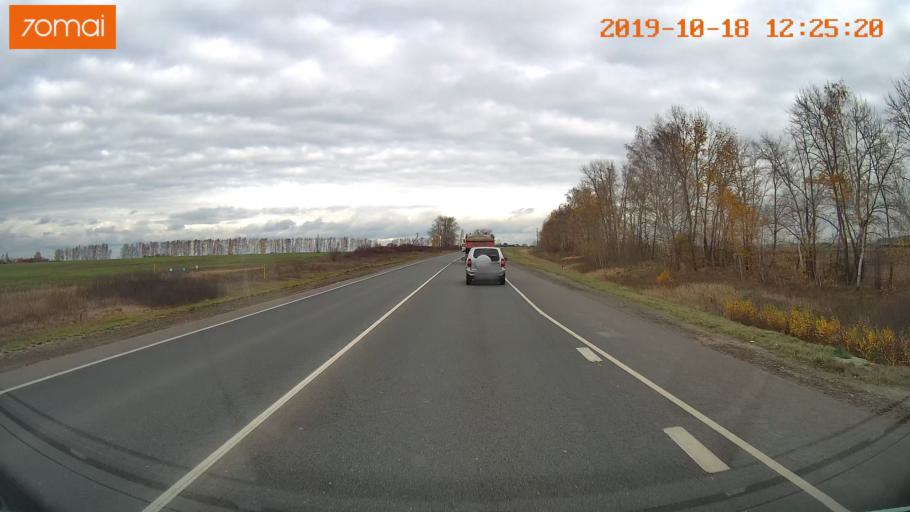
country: RU
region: Rjazan
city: Rybnoye
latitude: 54.5490
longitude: 39.5194
